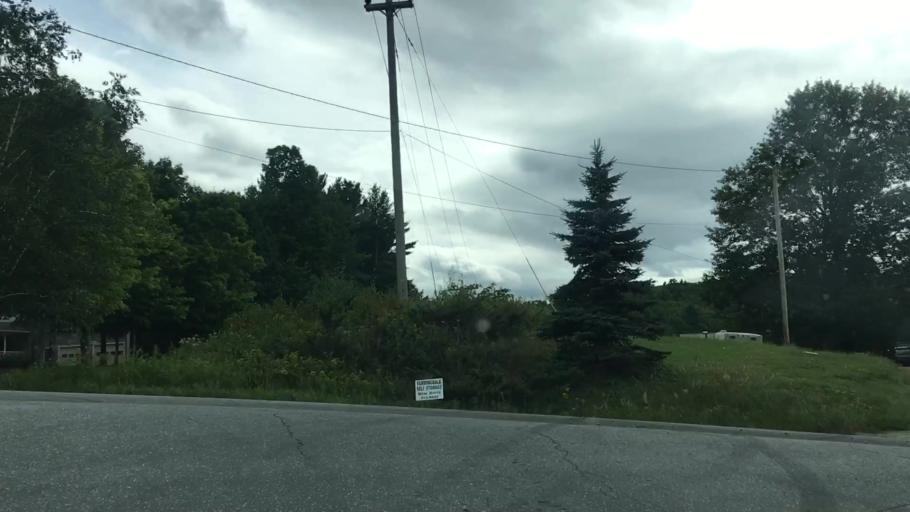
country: US
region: Maine
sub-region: Kennebec County
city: Hallowell
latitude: 44.2651
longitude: -69.8143
